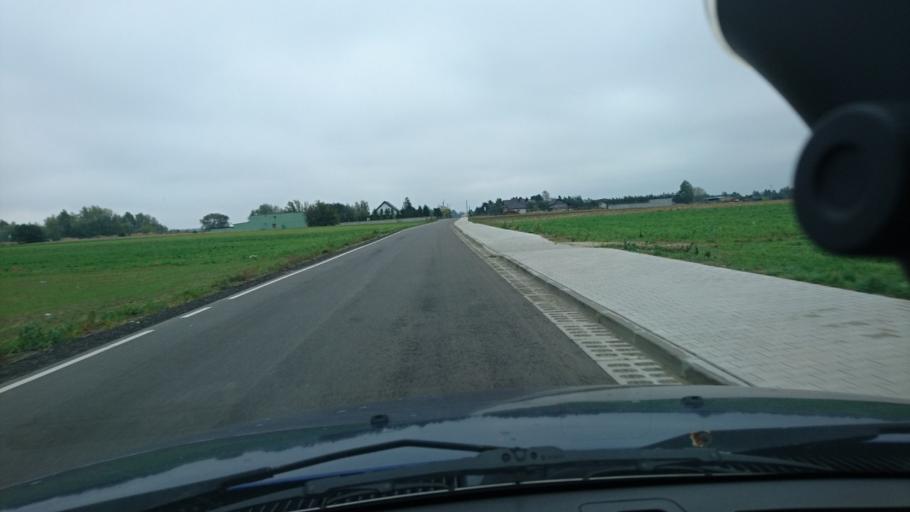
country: PL
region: Greater Poland Voivodeship
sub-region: Powiat ostrowski
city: Odolanow
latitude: 51.5738
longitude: 17.6071
